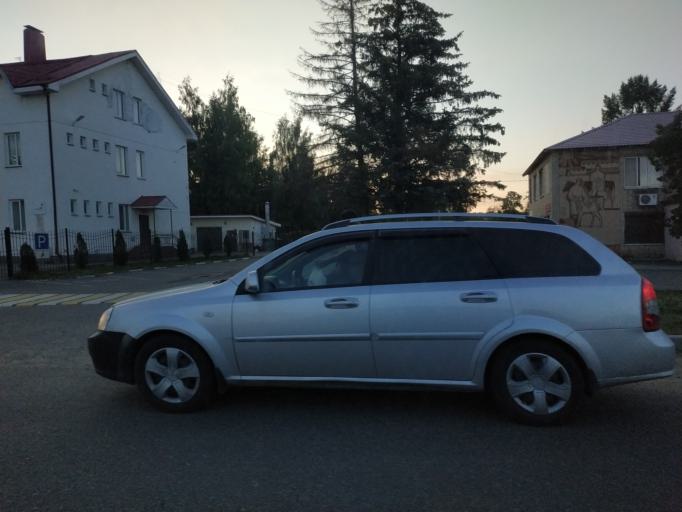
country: RU
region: Moskovskaya
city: Chernogolovka
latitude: 56.0621
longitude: 38.2556
